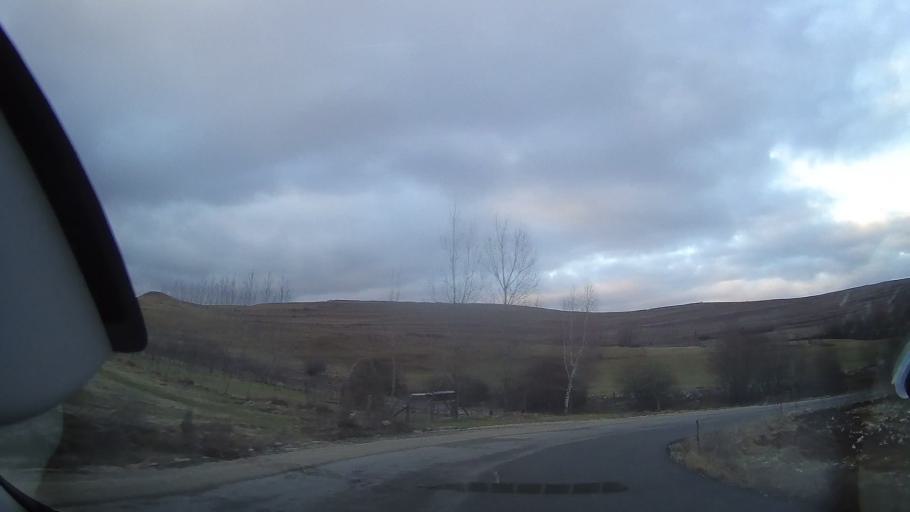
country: RO
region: Cluj
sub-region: Comuna Manastireni
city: Manastireni
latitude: 46.7807
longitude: 23.0673
